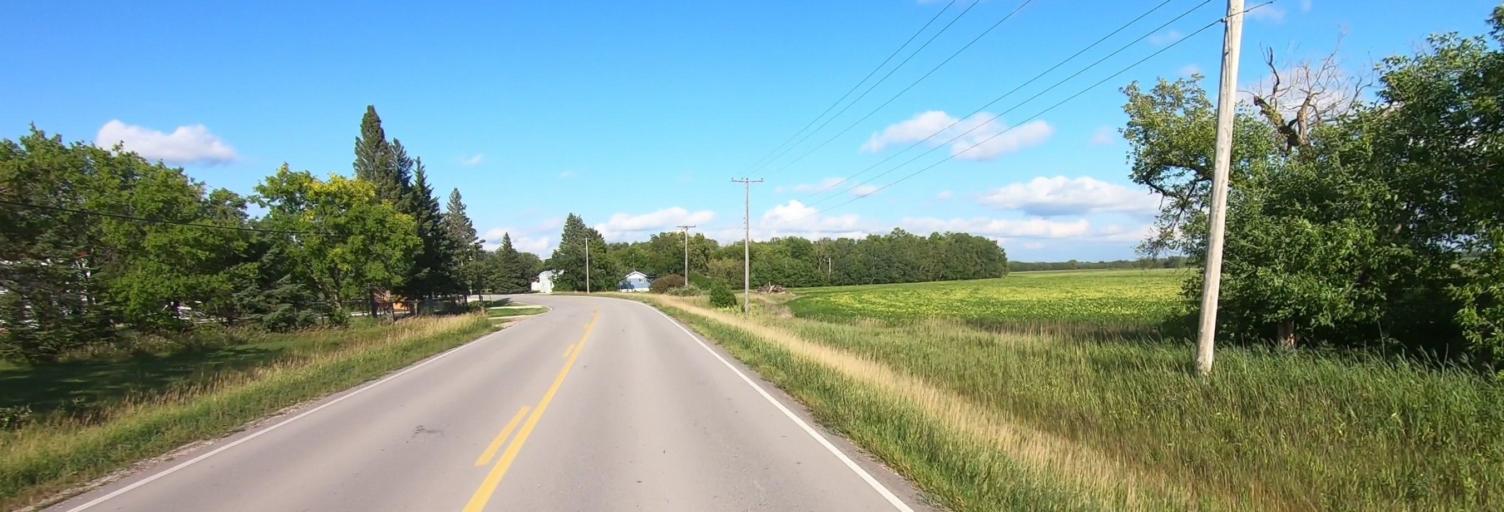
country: CA
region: Manitoba
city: Selkirk
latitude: 50.1139
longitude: -96.9044
